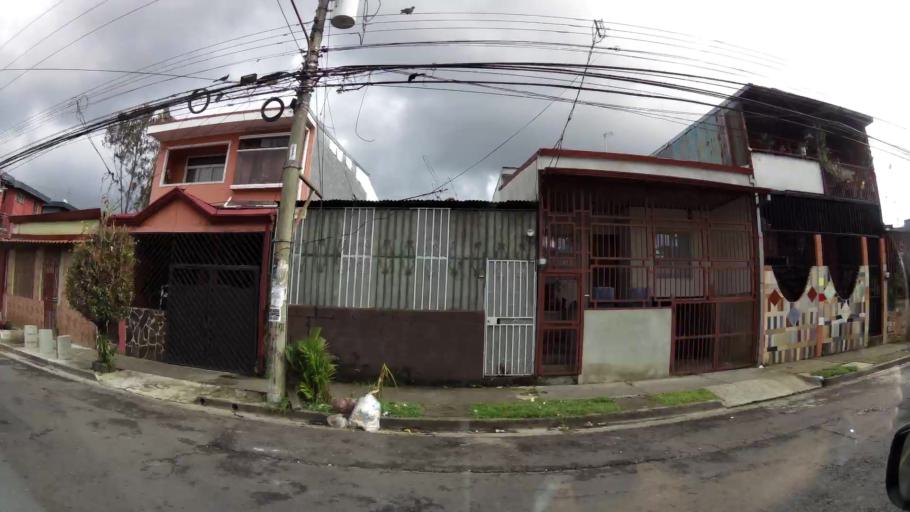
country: CR
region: San Jose
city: Curridabat
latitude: 9.9099
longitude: -84.0424
